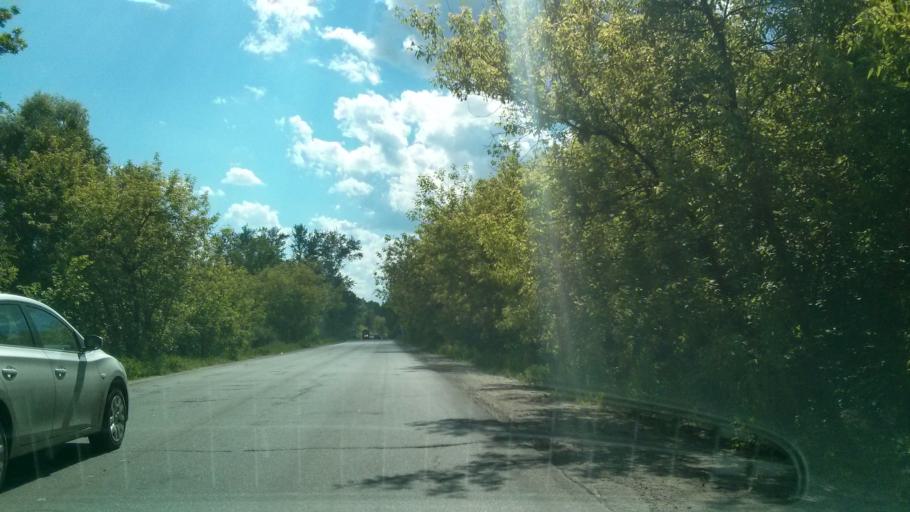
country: RU
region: Vladimir
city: Murom
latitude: 55.5518
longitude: 42.0021
